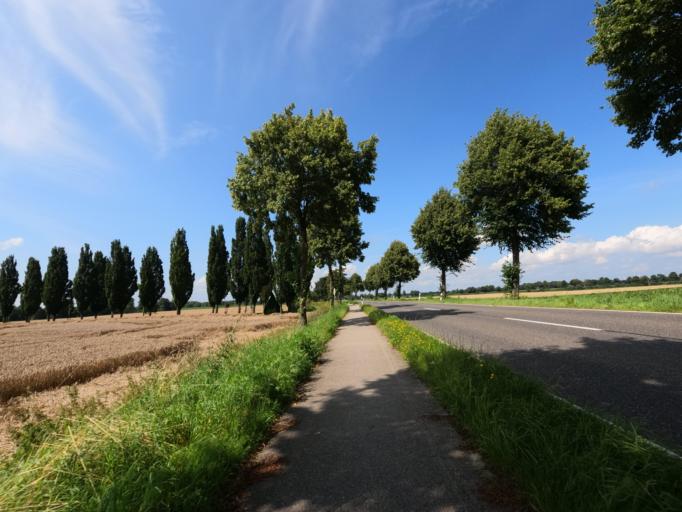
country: DE
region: North Rhine-Westphalia
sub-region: Regierungsbezirk Koln
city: Ubach-Palenberg
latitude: 50.9485
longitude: 6.1440
